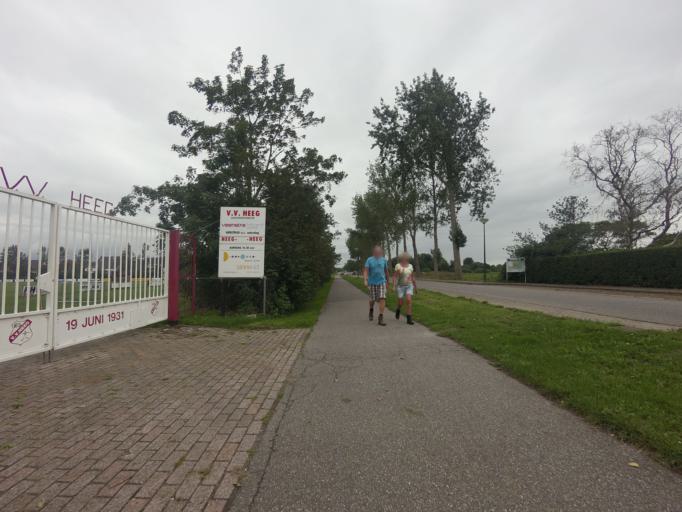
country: NL
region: Friesland
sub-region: Sudwest Fryslan
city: Heeg
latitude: 52.9753
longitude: 5.6055
